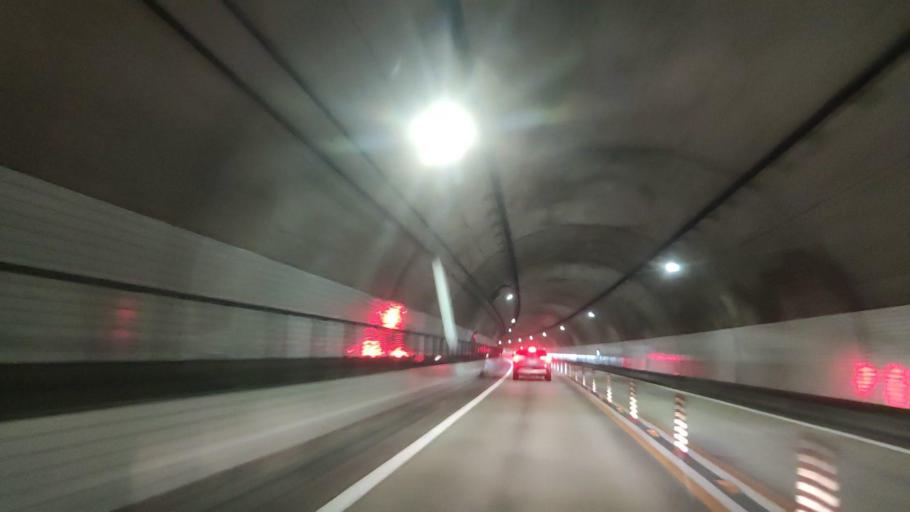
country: JP
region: Kyoto
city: Miyazu
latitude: 35.5582
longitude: 135.1243
